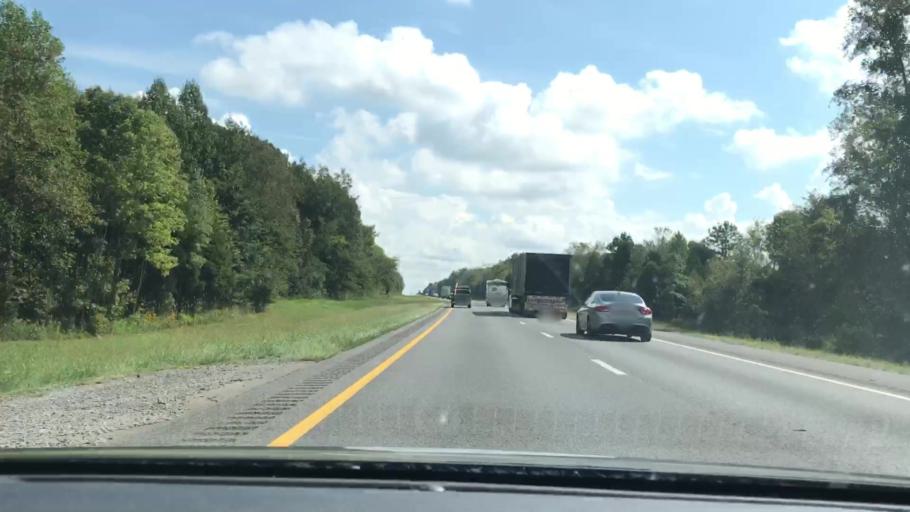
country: US
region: Kentucky
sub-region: Todd County
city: Guthrie
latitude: 36.5139
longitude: -87.2076
